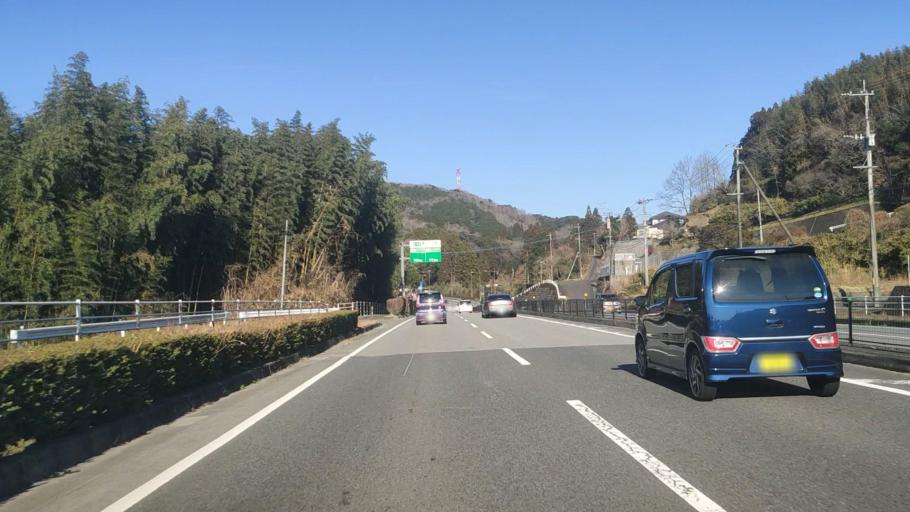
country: JP
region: Oita
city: Oita
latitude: 33.1069
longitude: 131.6551
